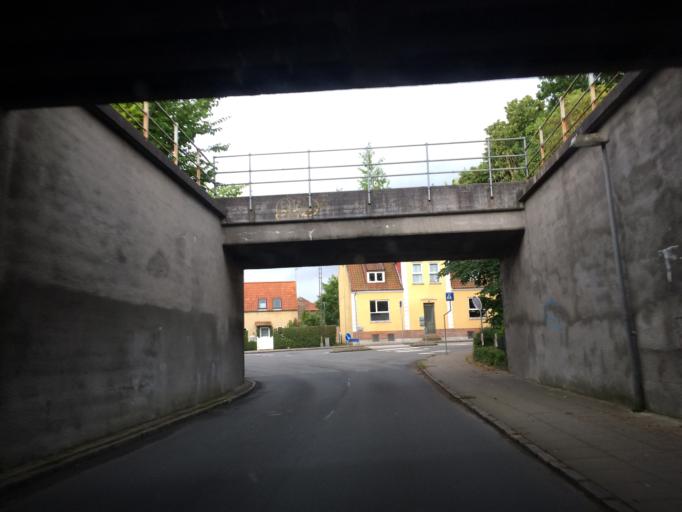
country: DK
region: Central Jutland
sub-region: Silkeborg Kommune
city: Silkeborg
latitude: 56.1639
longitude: 9.5353
